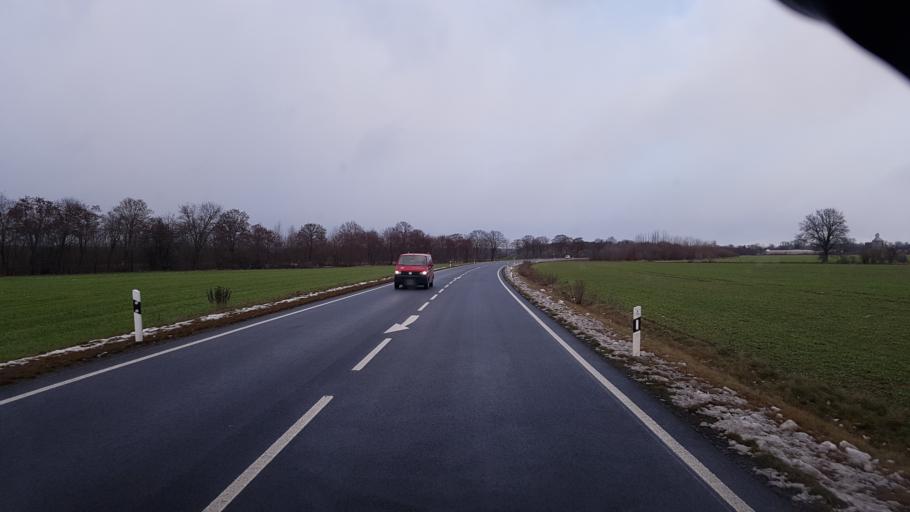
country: DE
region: Brandenburg
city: Schenkendobern
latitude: 51.8770
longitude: 14.6304
